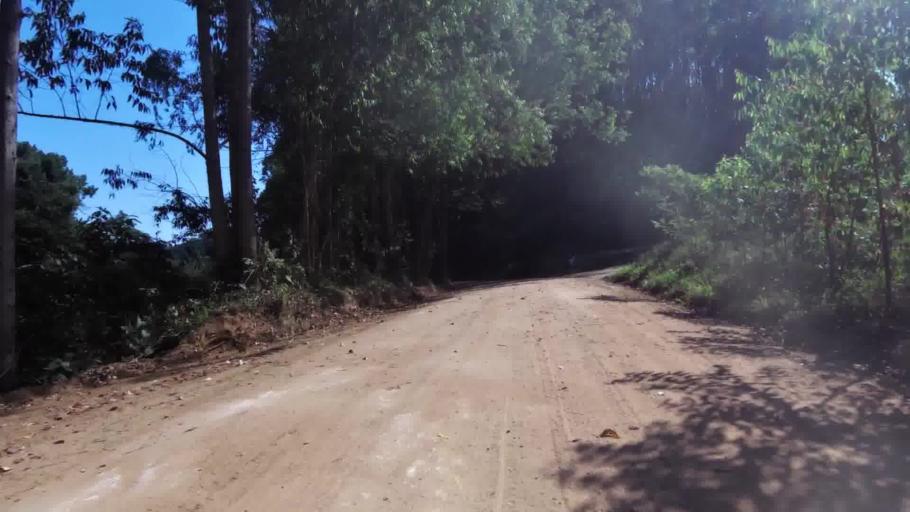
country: BR
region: Espirito Santo
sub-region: Alfredo Chaves
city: Alfredo Chaves
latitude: -20.5451
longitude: -40.8345
